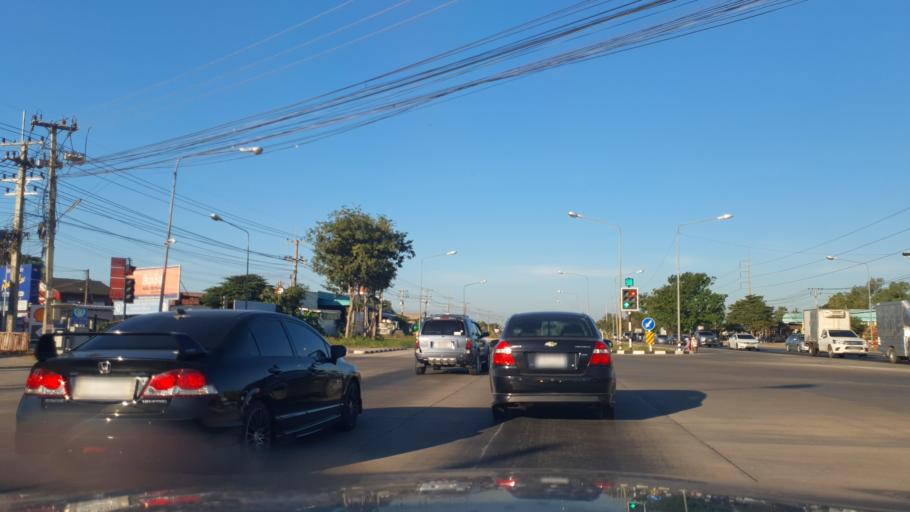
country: TH
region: Phitsanulok
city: Phitsanulok
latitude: 16.8642
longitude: 100.2797
